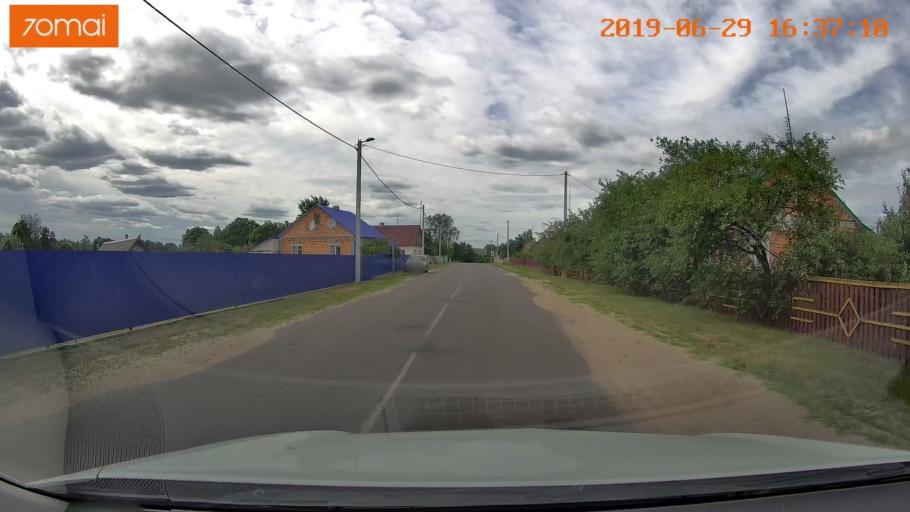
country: BY
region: Brest
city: Luninyets
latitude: 52.2255
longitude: 27.0229
